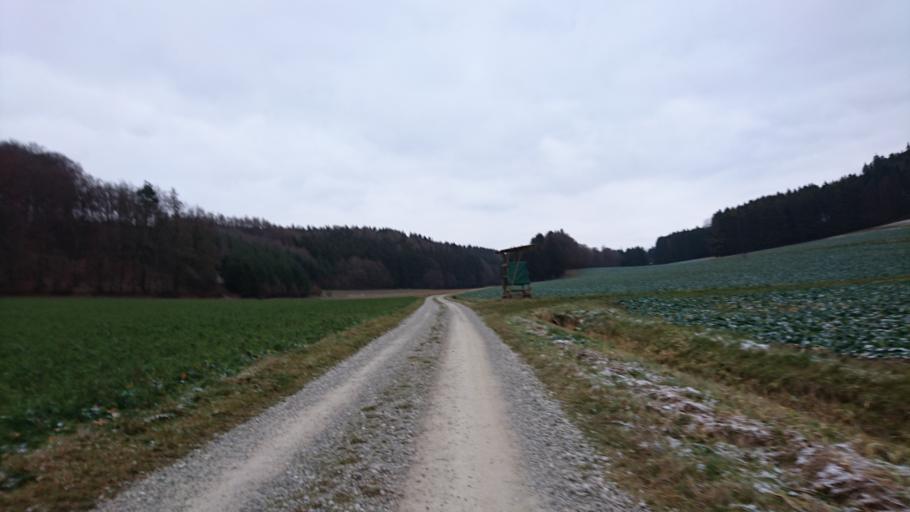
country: DE
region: Bavaria
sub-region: Swabia
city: Zusmarshausen
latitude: 48.4292
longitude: 10.6079
